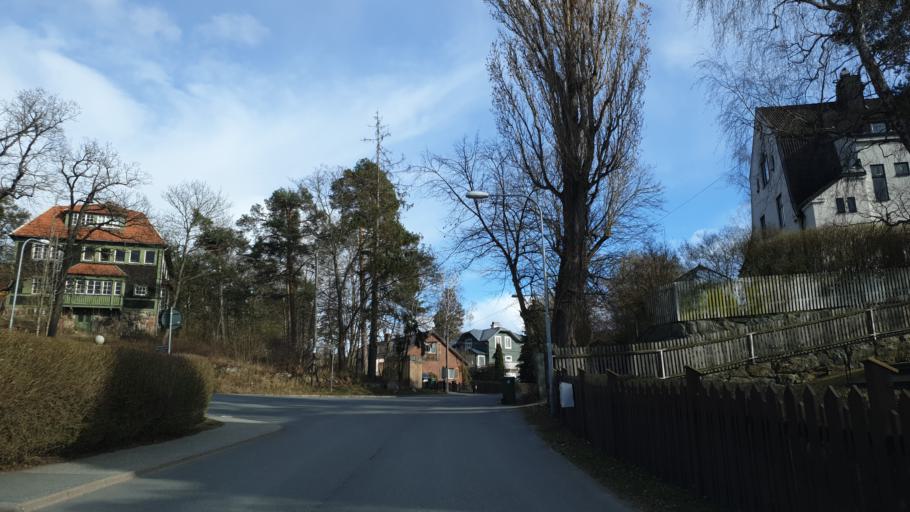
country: SE
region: Stockholm
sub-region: Lidingo
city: Lidingoe
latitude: 59.3684
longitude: 18.1260
